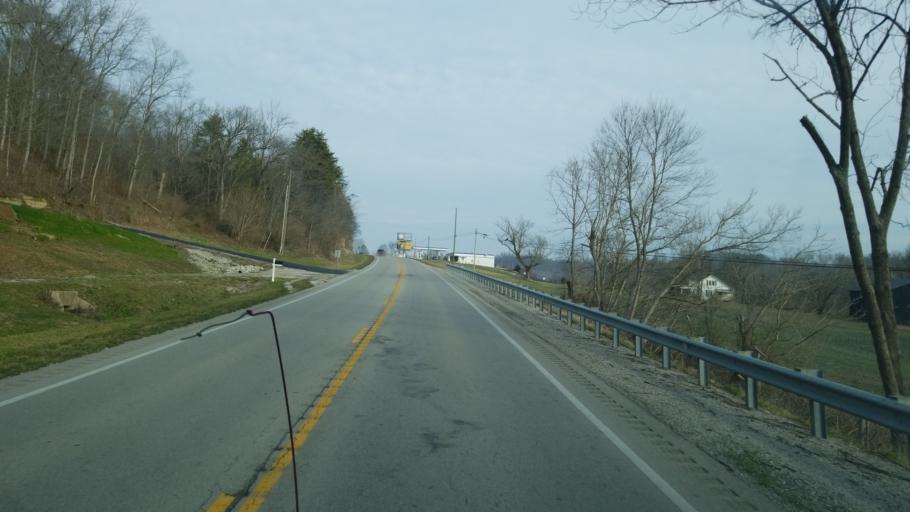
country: US
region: Kentucky
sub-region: Casey County
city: Liberty
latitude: 37.3587
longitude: -84.8676
